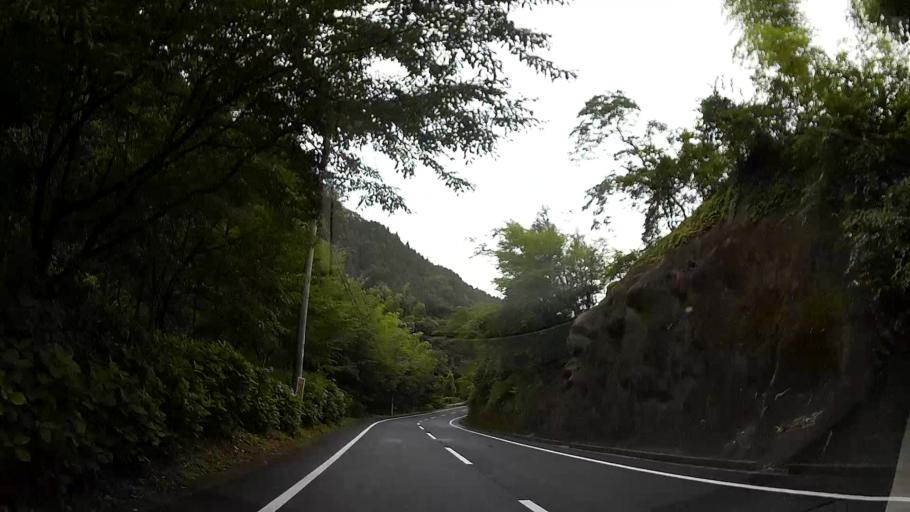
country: JP
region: Kumamoto
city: Kikuchi
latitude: 33.0826
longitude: 130.9431
